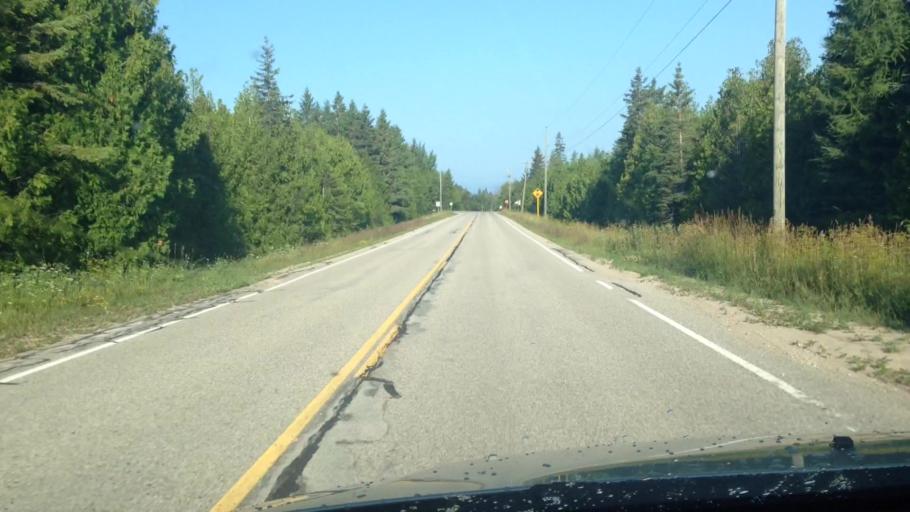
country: US
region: Michigan
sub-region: Mackinac County
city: Saint Ignace
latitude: 45.8921
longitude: -84.8293
